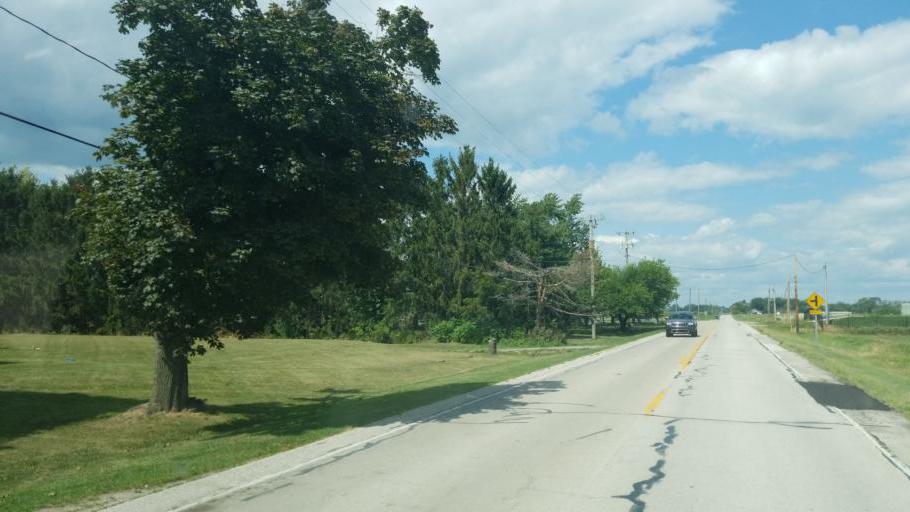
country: US
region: Ohio
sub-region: Lucas County
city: Curtice
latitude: 41.6449
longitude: -83.2733
